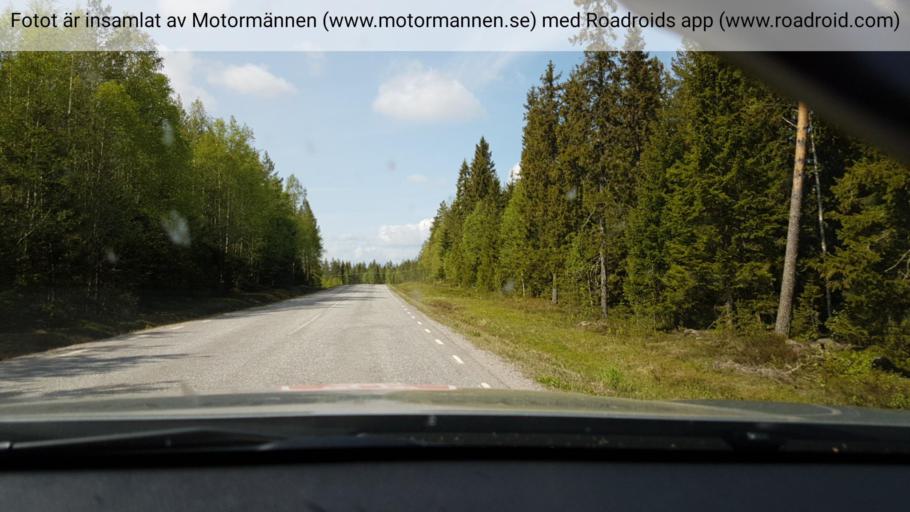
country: SE
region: Vaesterbotten
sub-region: Vannas Kommun
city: Vannasby
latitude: 63.8507
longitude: 19.9594
